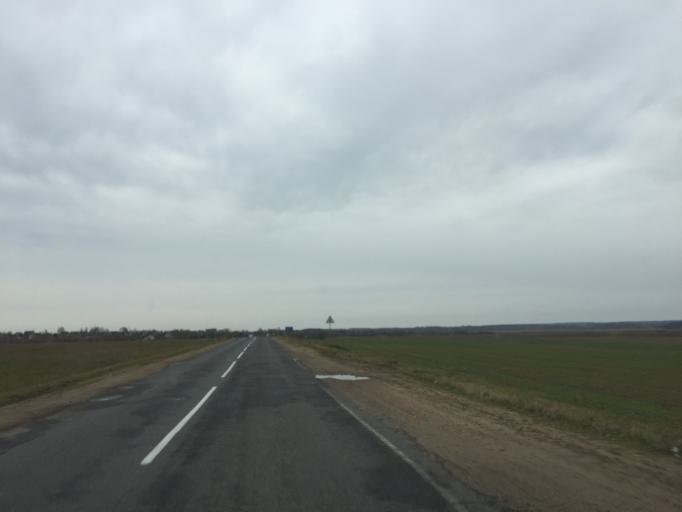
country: BY
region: Mogilev
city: Drybin
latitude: 54.1399
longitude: 31.1117
